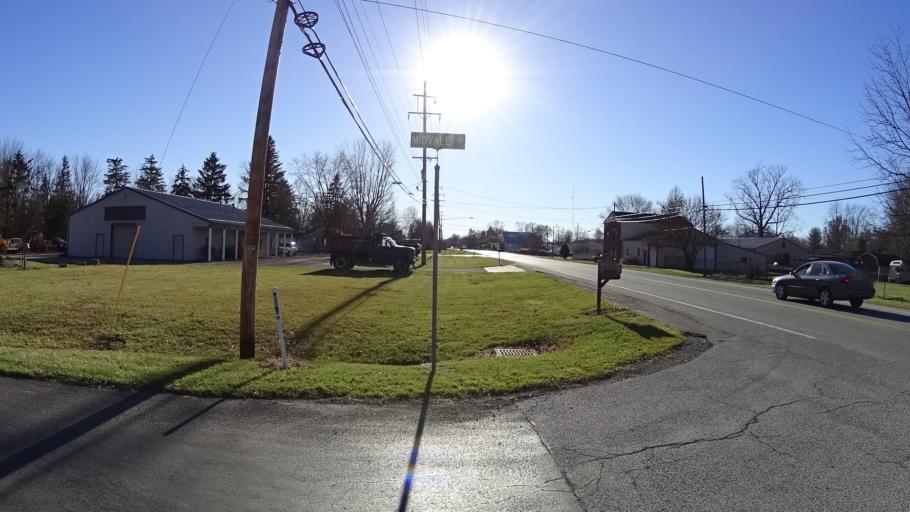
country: US
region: Ohio
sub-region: Lorain County
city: Elyria
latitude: 41.3276
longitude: -82.1322
